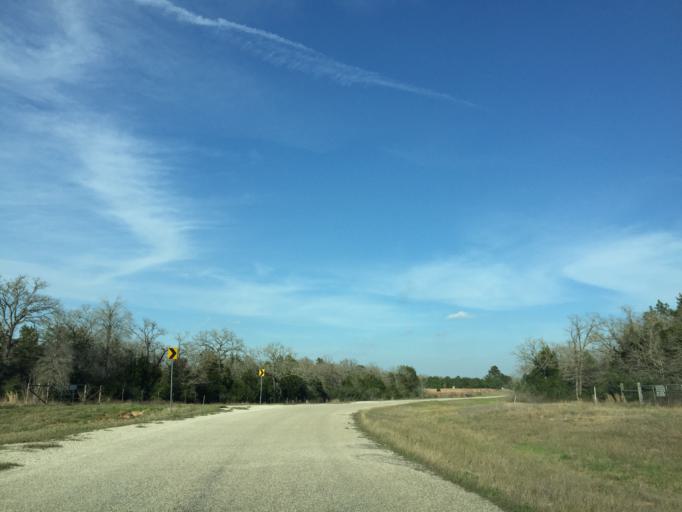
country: US
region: Texas
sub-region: Lee County
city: Lexington
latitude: 30.4525
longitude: -97.1677
